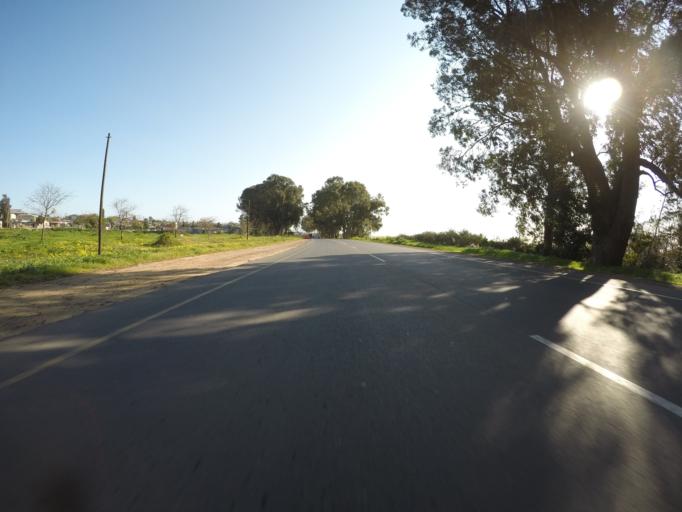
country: ZA
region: Western Cape
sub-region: City of Cape Town
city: Kraaifontein
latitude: -33.7793
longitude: 18.7193
